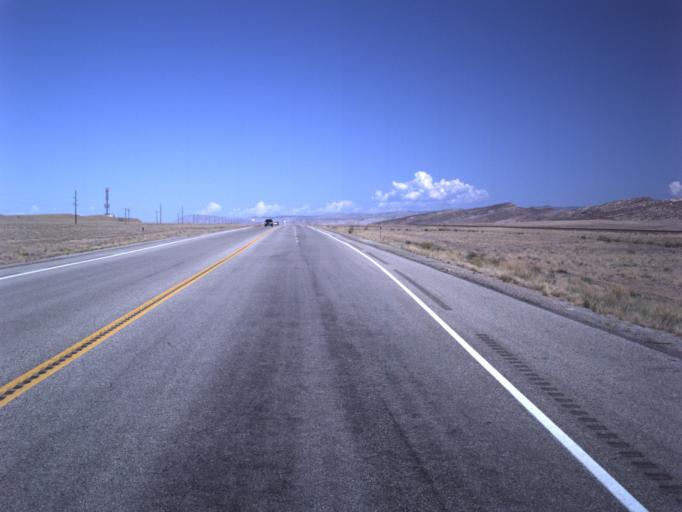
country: US
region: Utah
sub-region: Grand County
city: Moab
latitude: 38.7996
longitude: -109.7627
